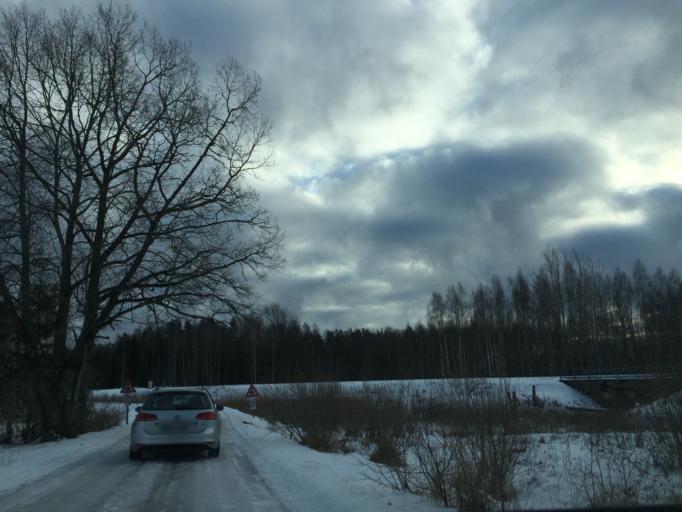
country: LV
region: Lielvarde
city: Lielvarde
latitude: 56.5752
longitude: 24.7979
